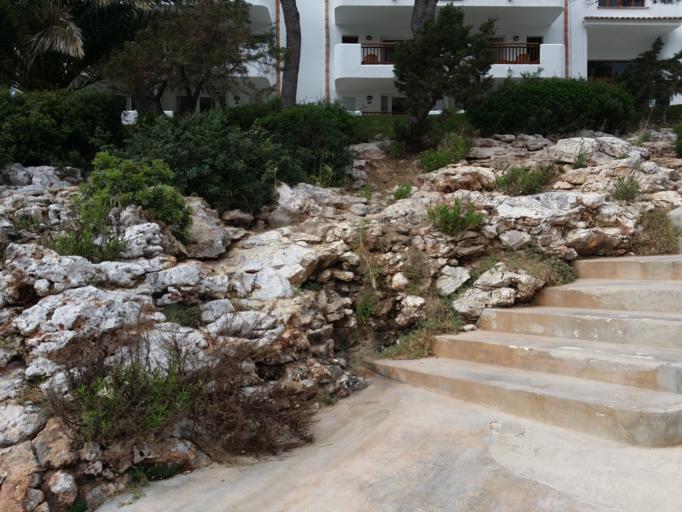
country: ES
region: Balearic Islands
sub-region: Illes Balears
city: Santanyi
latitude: 39.3767
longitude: 3.2388
